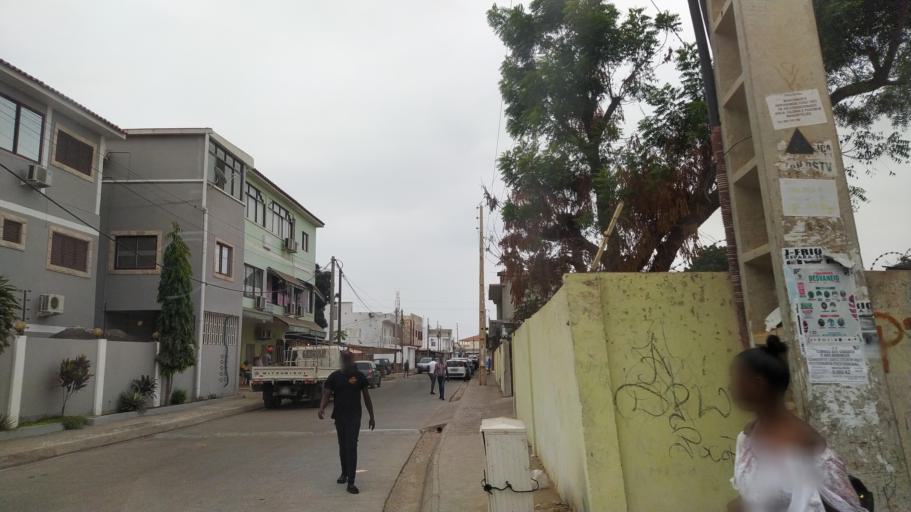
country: AO
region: Luanda
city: Luanda
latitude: -8.8878
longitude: 13.1832
